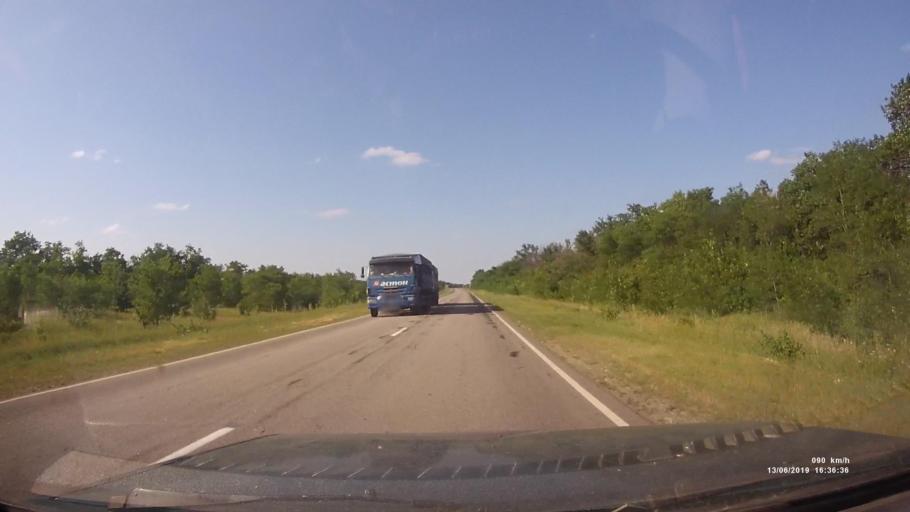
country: RU
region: Rostov
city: Kazanskaya
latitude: 49.8968
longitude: 41.3071
